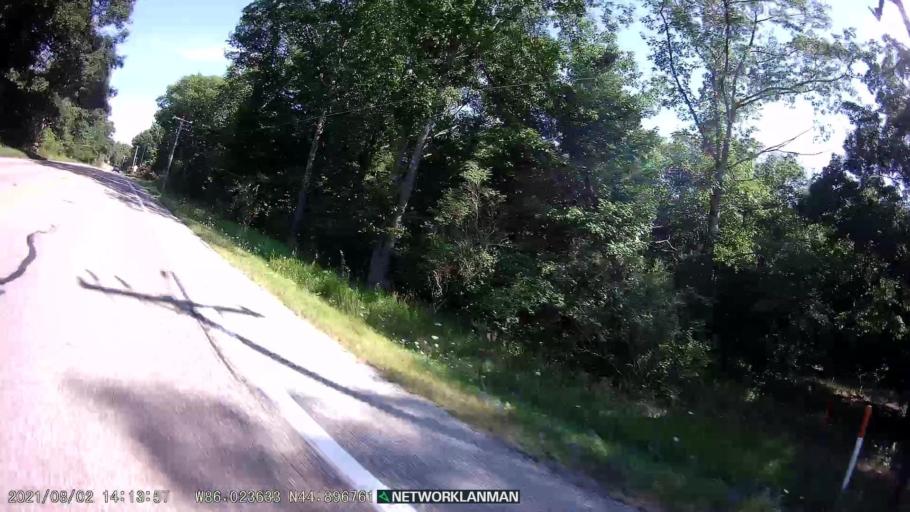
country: US
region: Michigan
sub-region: Benzie County
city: Beulah
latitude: 44.8967
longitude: -86.0234
